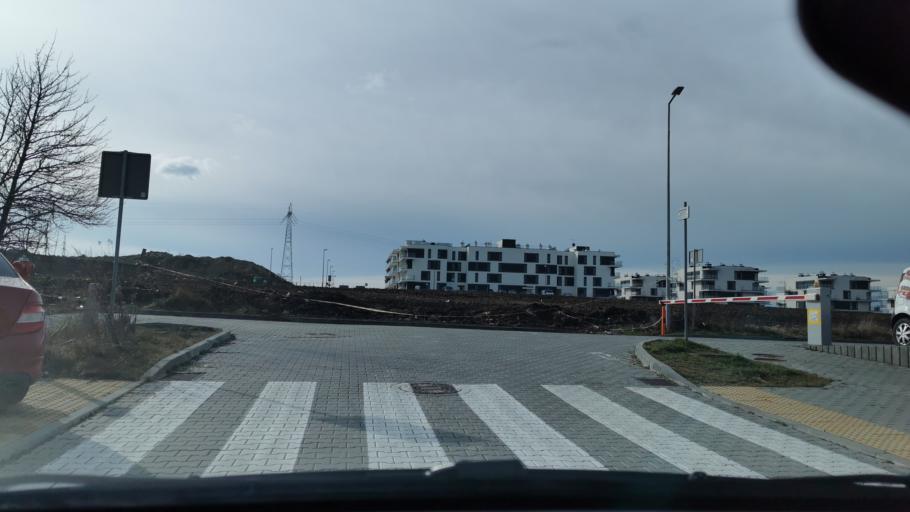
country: PL
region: Lublin Voivodeship
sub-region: Powiat lubelski
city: Lublin
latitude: 51.1981
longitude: 22.5457
